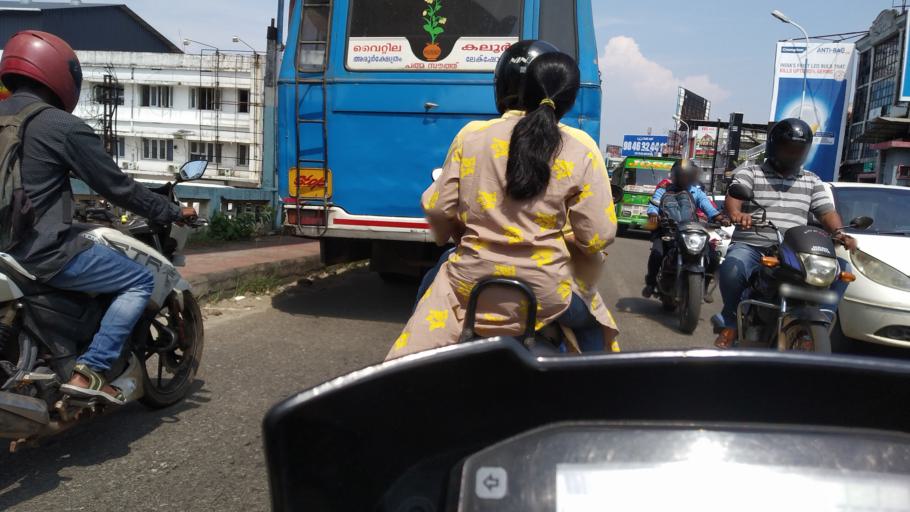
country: IN
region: Kerala
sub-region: Ernakulam
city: Cochin
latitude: 9.9653
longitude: 76.2928
